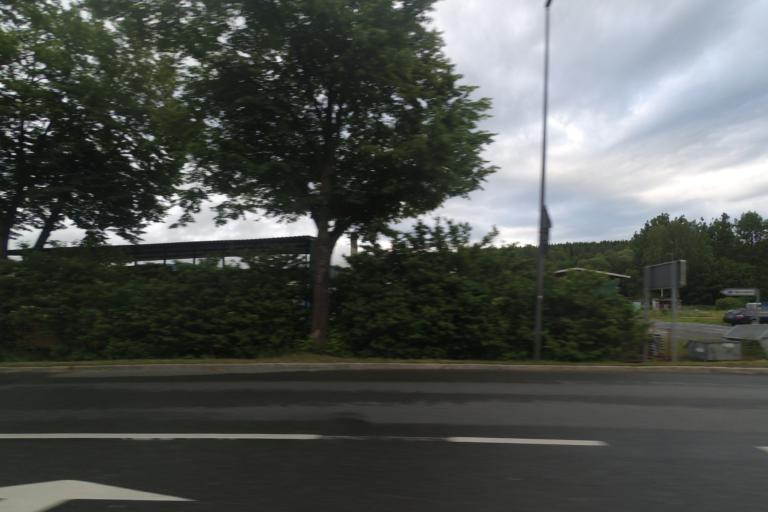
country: DE
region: Bavaria
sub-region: Upper Franconia
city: Marktrodach
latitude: 50.2427
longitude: 11.3829
